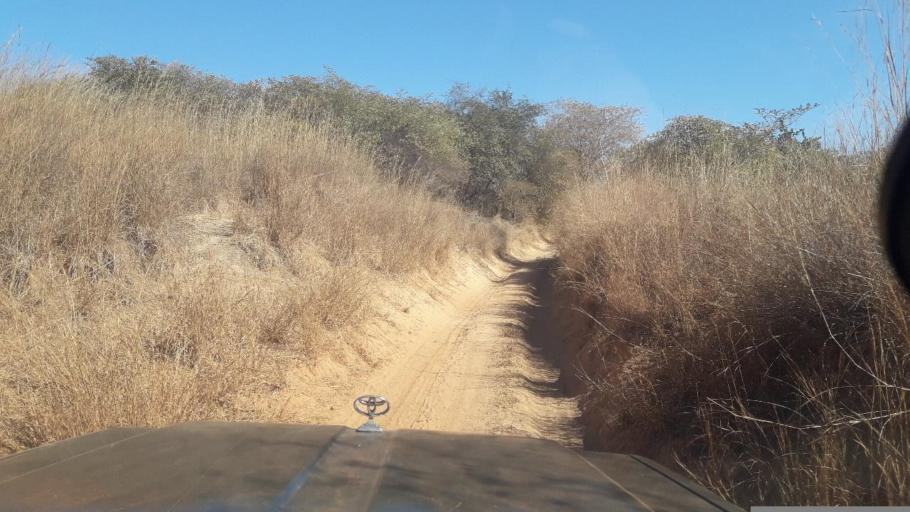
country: MG
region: Boeny
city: Sitampiky
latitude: -16.3122
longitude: 45.6305
